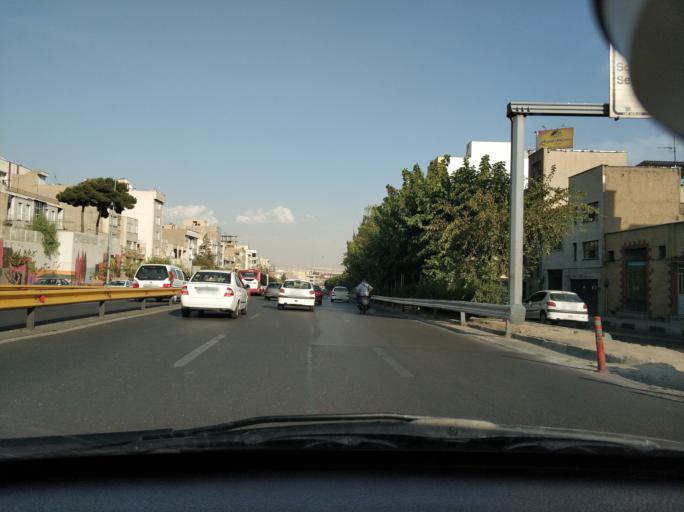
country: IR
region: Tehran
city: Tehran
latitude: 35.7426
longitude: 51.4397
